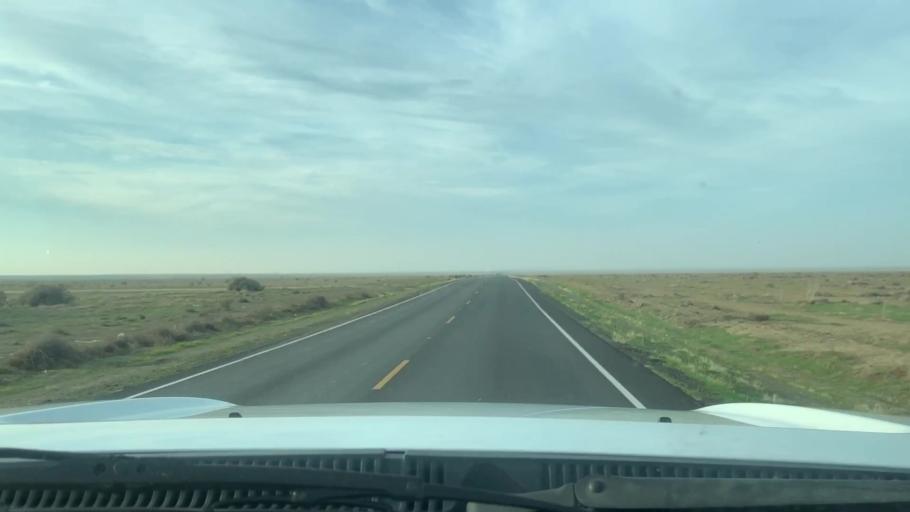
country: US
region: California
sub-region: Kern County
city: Lost Hills
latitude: 35.5670
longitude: -119.8090
